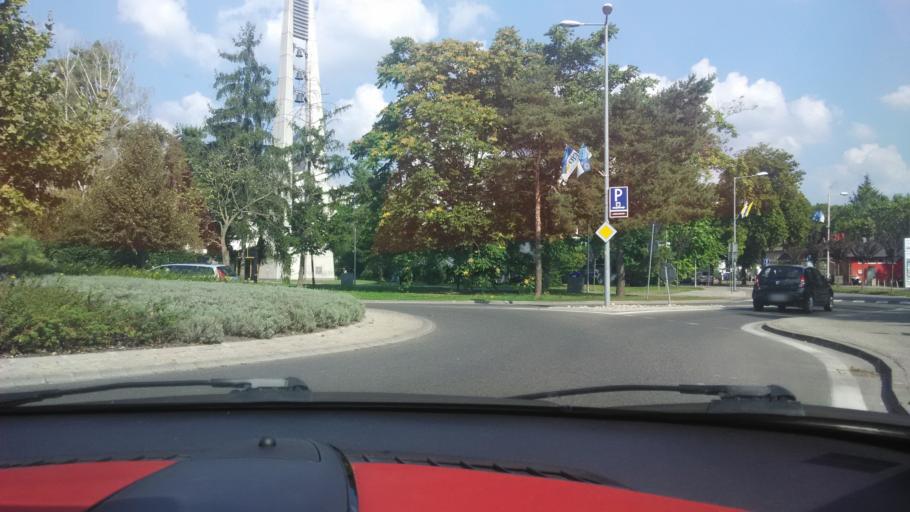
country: SK
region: Trnavsky
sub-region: Okres Trnava
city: Piestany
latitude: 48.5870
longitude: 17.8332
